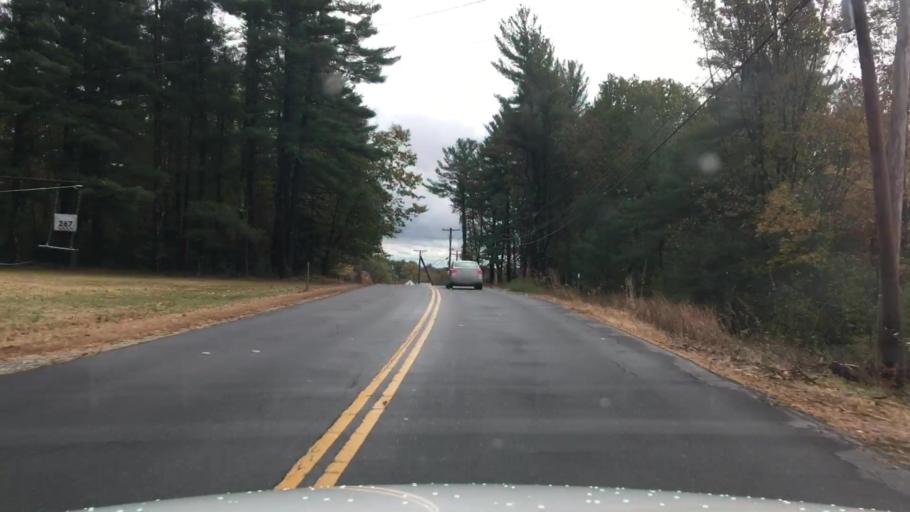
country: US
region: New Hampshire
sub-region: Strafford County
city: Lee
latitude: 43.0942
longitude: -70.9831
